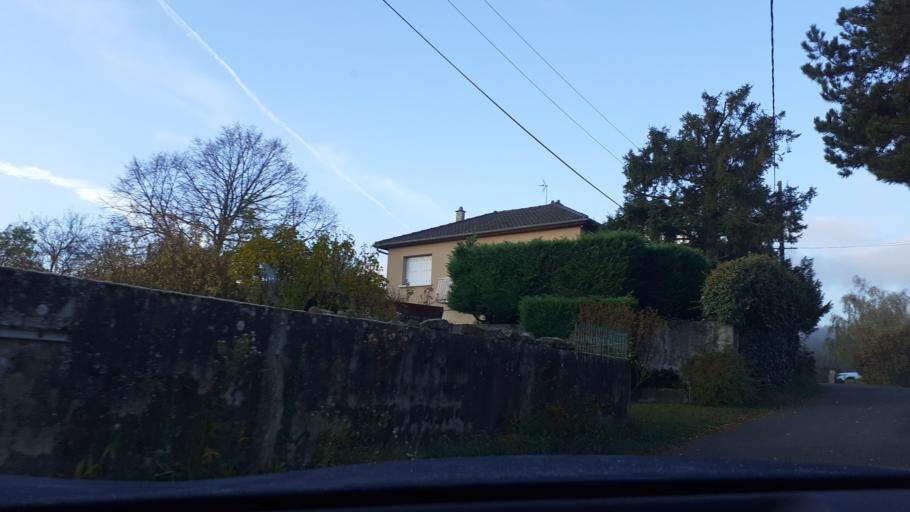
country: FR
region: Rhone-Alpes
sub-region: Departement du Rhone
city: Charnay
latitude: 45.9107
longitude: 4.6718
